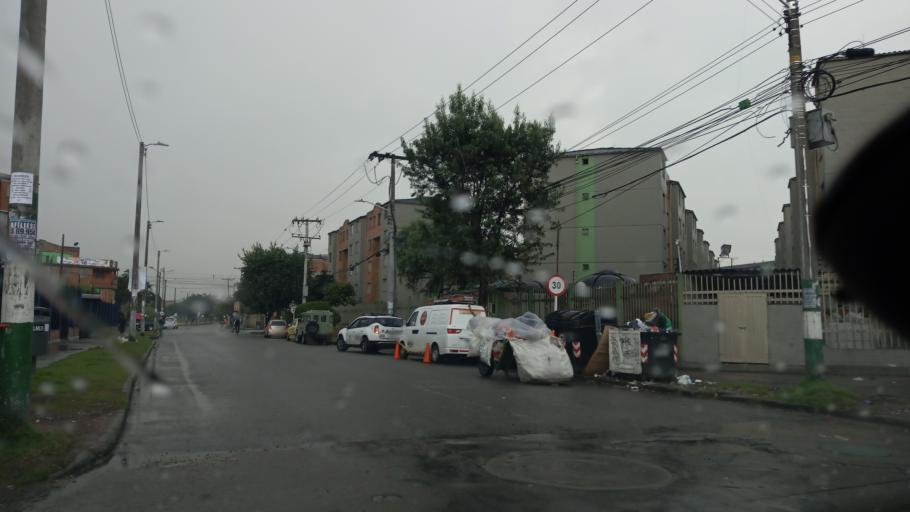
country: CO
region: Cundinamarca
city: Funza
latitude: 4.6759
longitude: -74.1521
